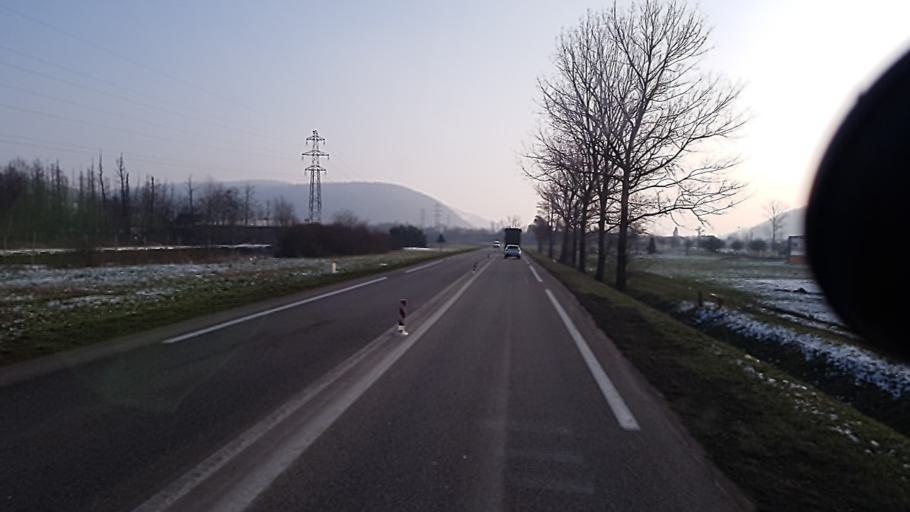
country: FR
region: Alsace
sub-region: Departement du Bas-Rhin
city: Dinsheim-sur-Bruche
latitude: 48.5360
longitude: 7.4163
